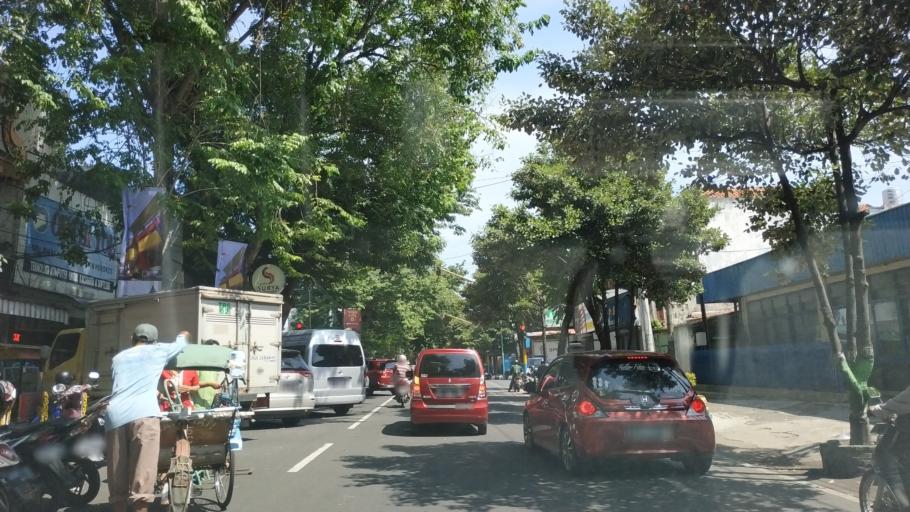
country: ID
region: Central Java
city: Pati
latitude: -6.7527
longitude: 111.0375
